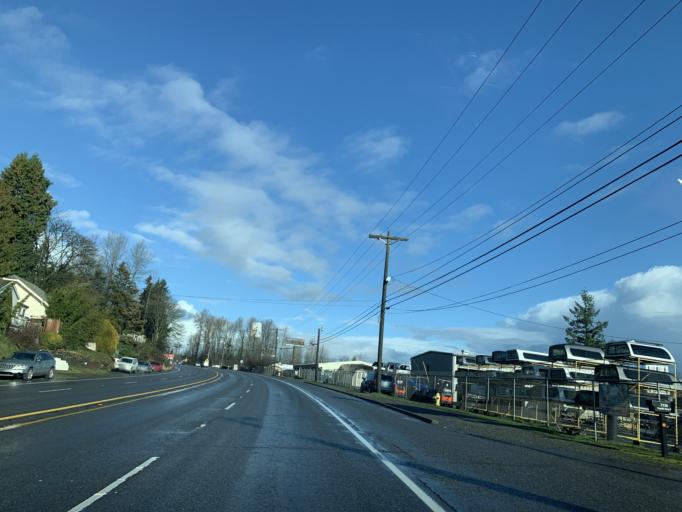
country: US
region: Washington
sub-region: Pierce County
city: Fife Heights
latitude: 47.2471
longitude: -122.3351
